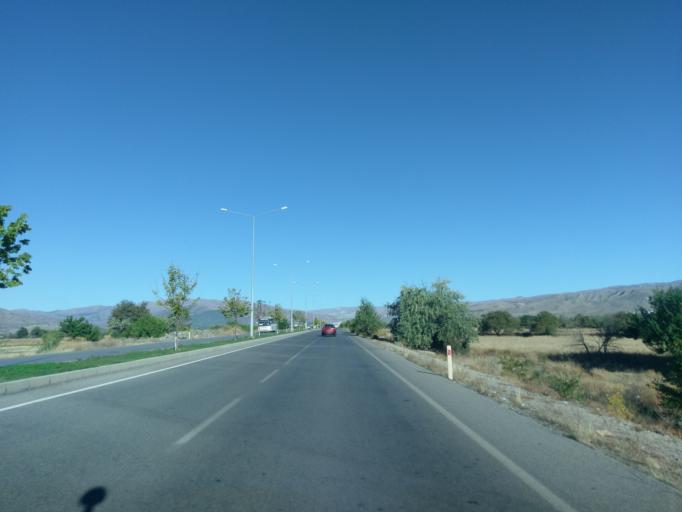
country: TR
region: Erzincan
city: Erzincan
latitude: 39.7813
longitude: 39.4083
